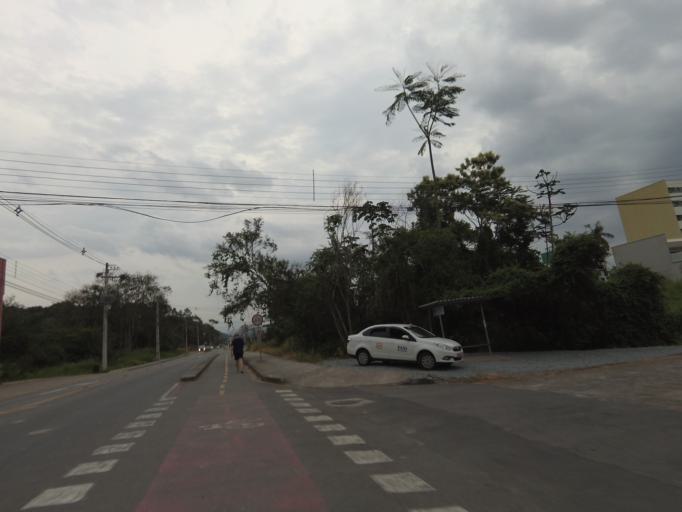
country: BR
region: Santa Catarina
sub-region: Blumenau
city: Blumenau
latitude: -26.8845
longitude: -49.0628
